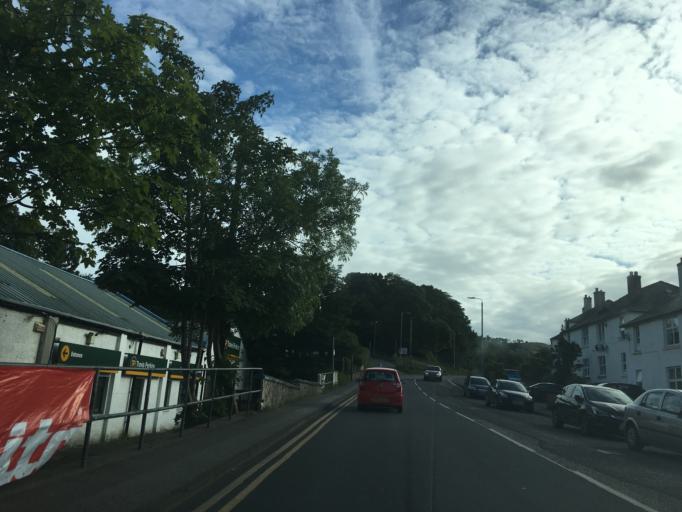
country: GB
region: Scotland
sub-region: Argyll and Bute
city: Oban
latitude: 56.4043
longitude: -5.4707
